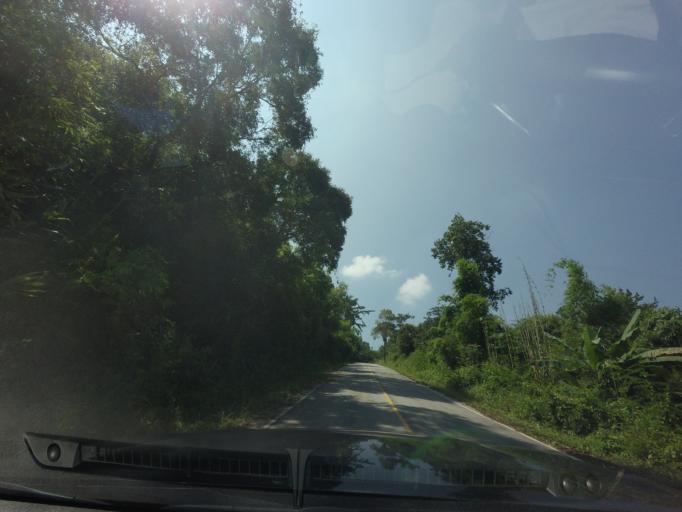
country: TH
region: Loei
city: Na Haeo
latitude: 17.5654
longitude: 100.9499
